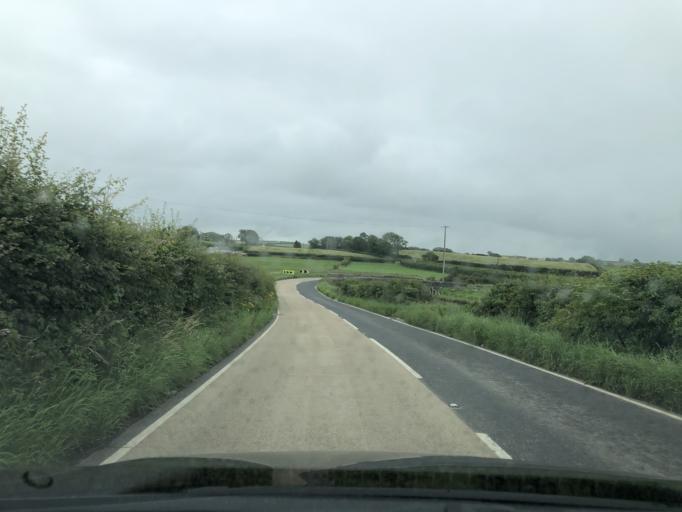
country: GB
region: Northern Ireland
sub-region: Down District
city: Dundrum
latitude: 54.2863
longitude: -5.8156
